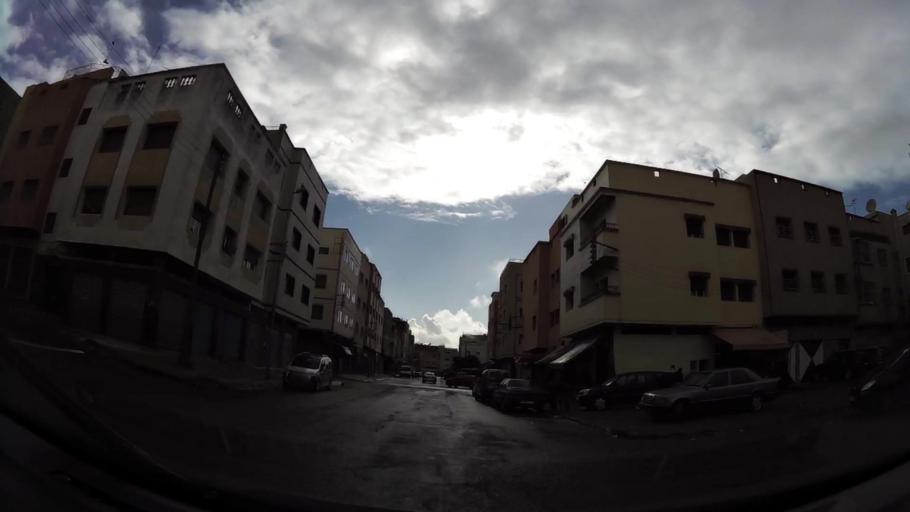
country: MA
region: Grand Casablanca
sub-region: Casablanca
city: Casablanca
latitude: 33.5458
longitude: -7.5926
